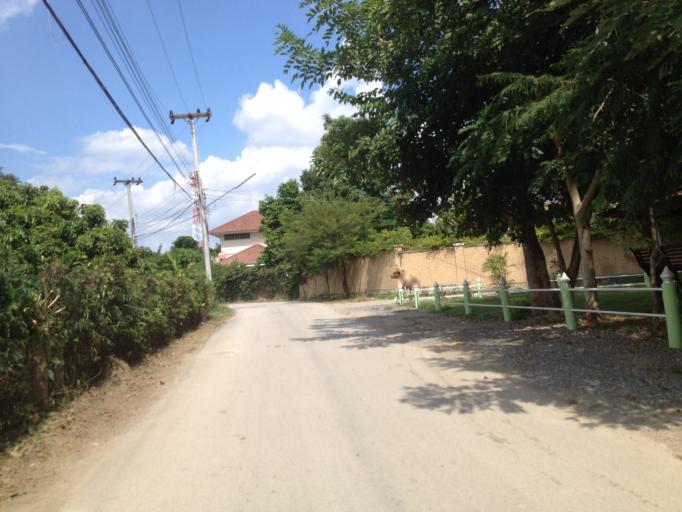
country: TH
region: Chiang Mai
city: Hang Dong
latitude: 18.7194
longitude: 98.9190
